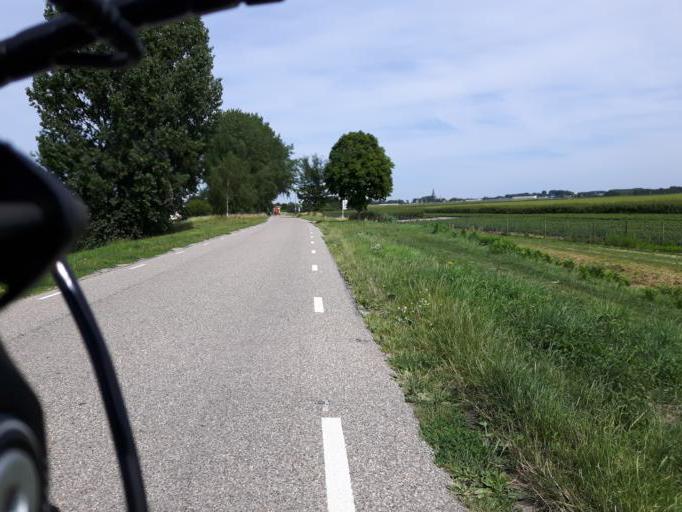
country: NL
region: North Brabant
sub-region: Gemeente Steenbergen
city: Steenbergen
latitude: 51.5896
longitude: 4.2810
